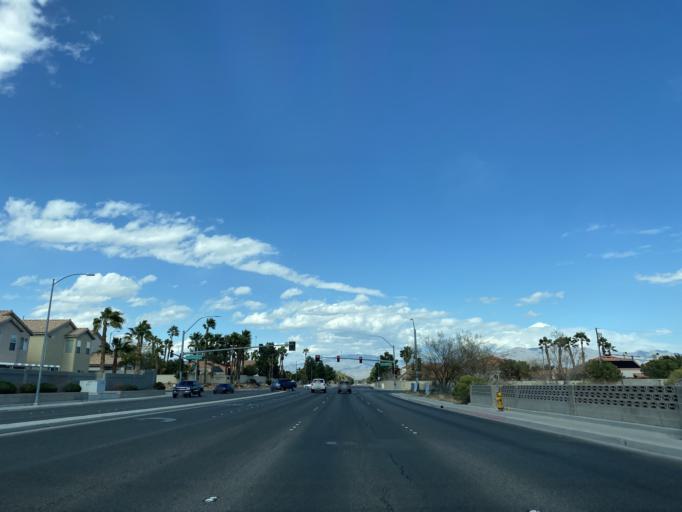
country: US
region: Nevada
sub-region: Clark County
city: Spring Valley
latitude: 36.2321
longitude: -115.2606
